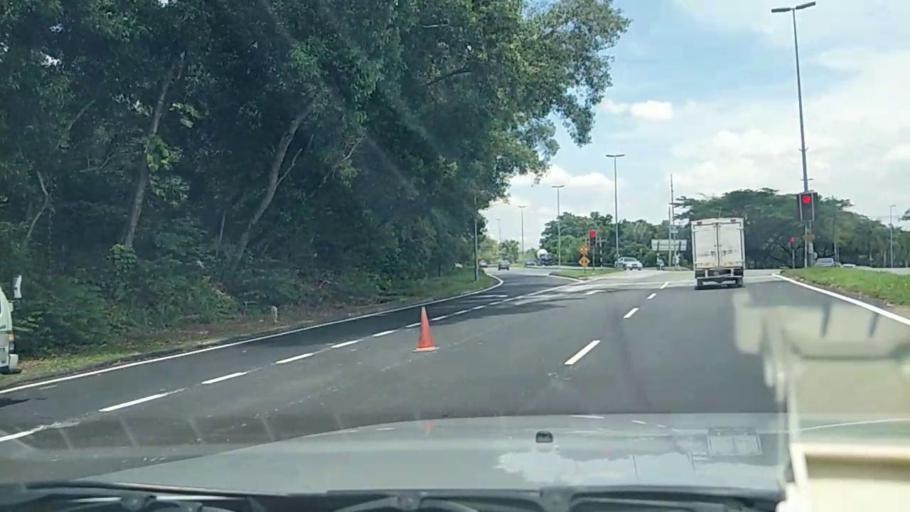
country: MY
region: Putrajaya
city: Putrajaya
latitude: 2.9636
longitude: 101.6168
